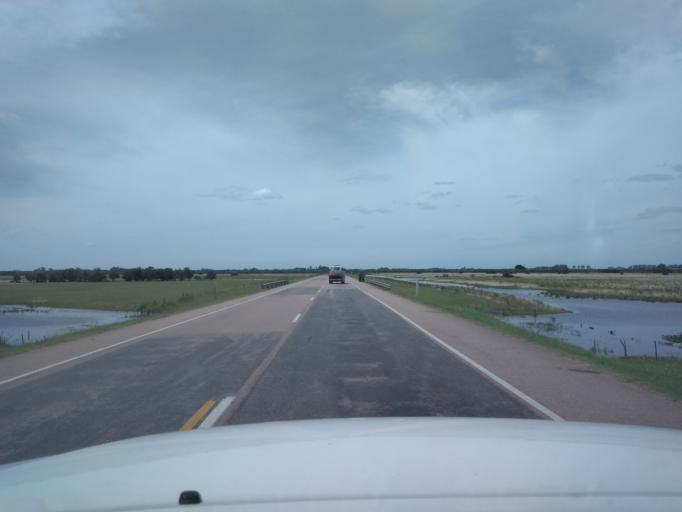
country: UY
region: Canelones
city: Canelones
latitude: -34.3813
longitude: -56.2526
